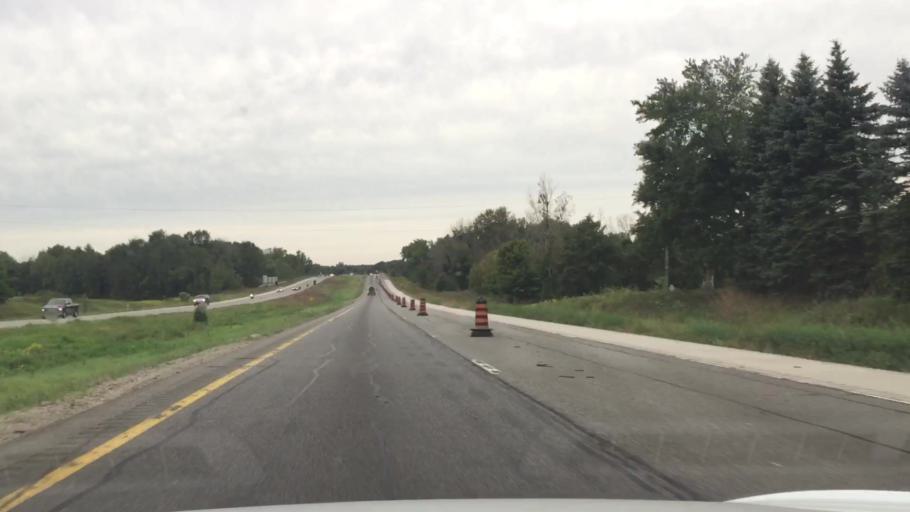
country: CA
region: Ontario
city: Delaware
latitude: 42.9355
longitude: -81.4823
